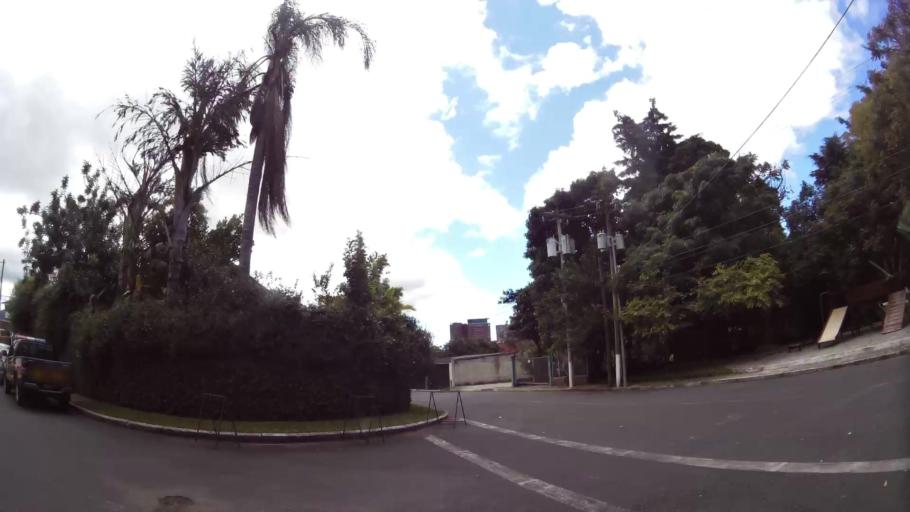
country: GT
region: Guatemala
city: Guatemala City
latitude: 14.6096
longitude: -90.5086
